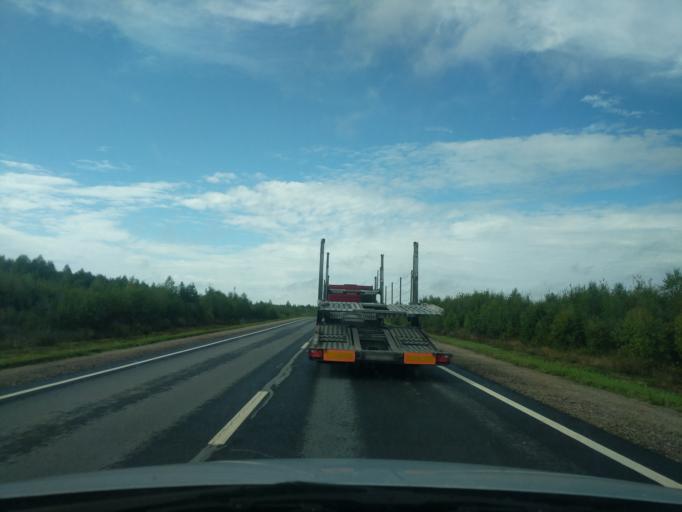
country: RU
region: Kostroma
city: Sudislavl'
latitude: 57.8213
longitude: 41.9094
